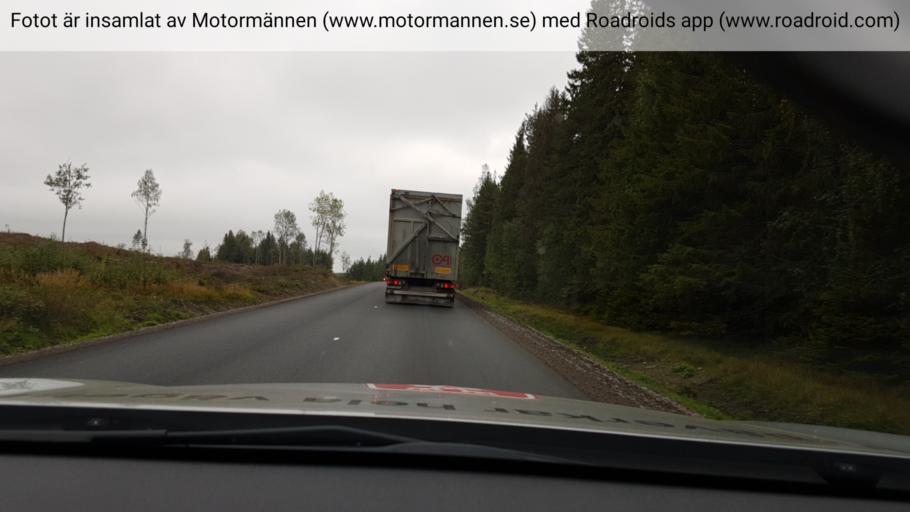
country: SE
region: Vaesterbotten
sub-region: Skelleftea Kommun
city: Burtraesk
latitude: 64.3759
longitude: 20.5079
